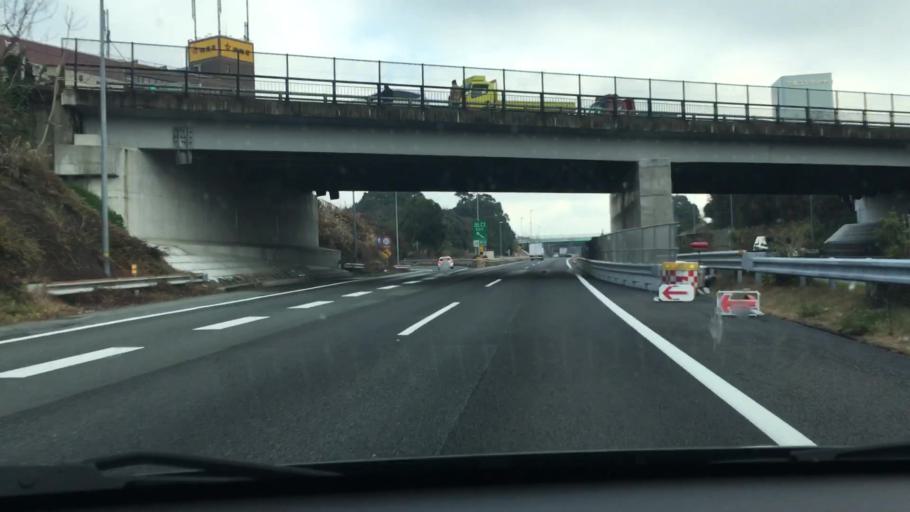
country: JP
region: Kumamoto
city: Kumamoto
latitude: 32.8368
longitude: 130.7778
